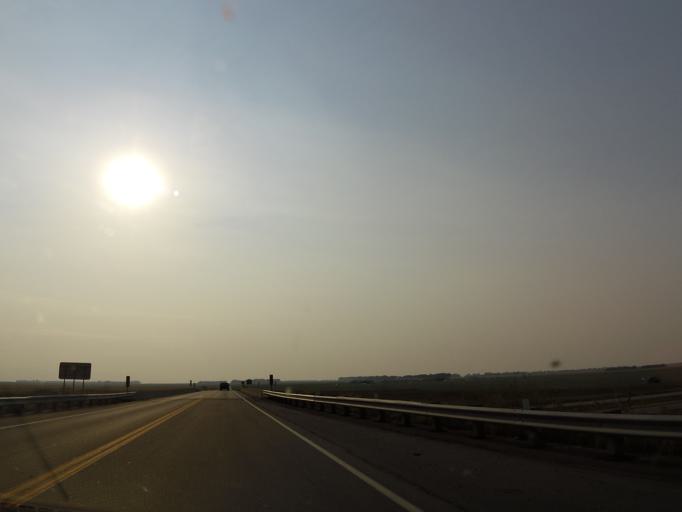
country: US
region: North Dakota
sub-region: Traill County
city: Hillsboro
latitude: 47.3529
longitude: -97.0487
